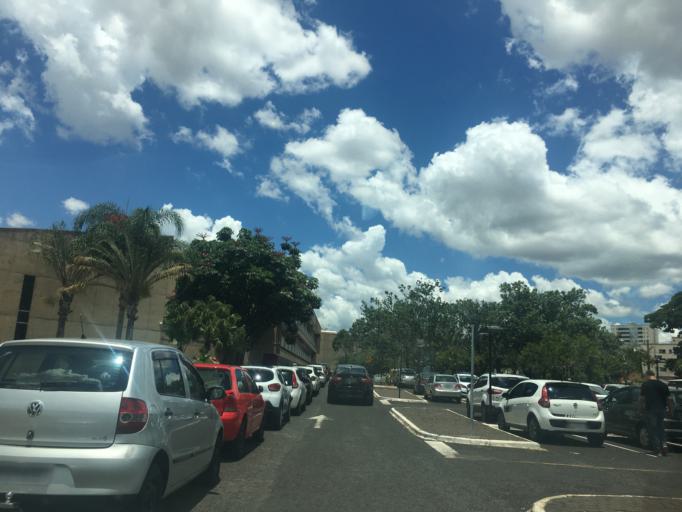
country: BR
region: Minas Gerais
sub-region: Uberlandia
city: Uberlandia
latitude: -18.9128
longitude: -48.2574
